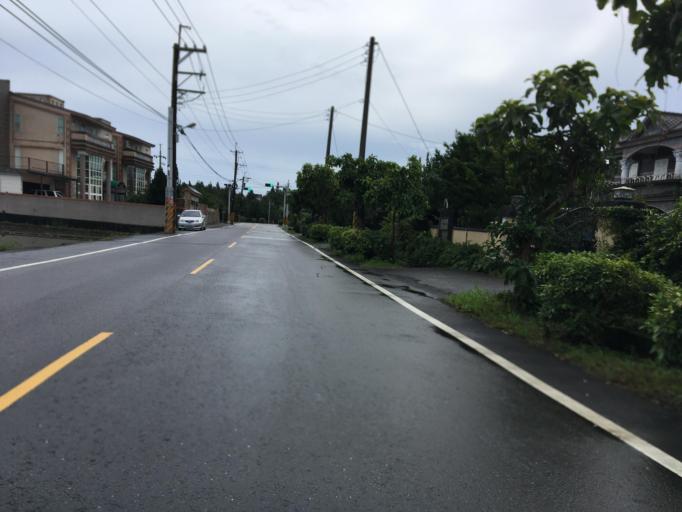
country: TW
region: Taiwan
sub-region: Yilan
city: Yilan
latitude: 24.6675
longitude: 121.7896
